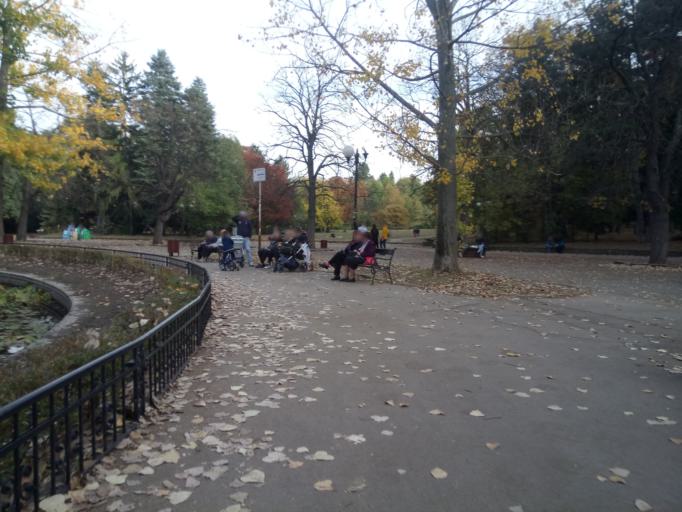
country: BG
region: Sofia-Capital
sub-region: Stolichna Obshtina
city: Sofia
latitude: 42.6847
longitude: 23.3421
